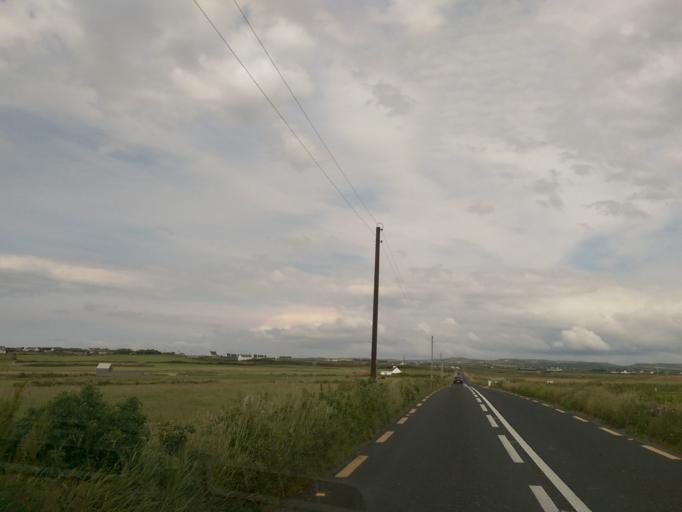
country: IE
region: Munster
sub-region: An Clar
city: Kilrush
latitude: 52.8229
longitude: -9.4474
